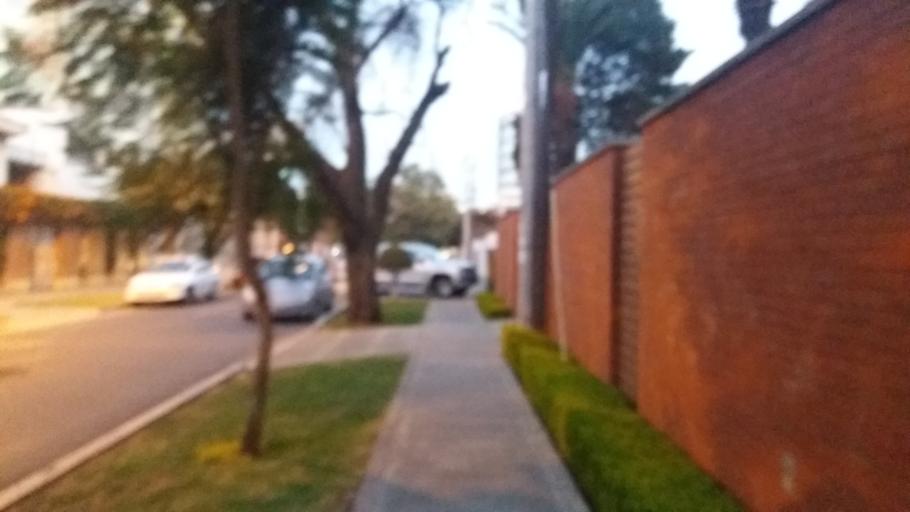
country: BO
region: Cochabamba
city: Cochabamba
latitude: -17.3846
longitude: -66.1519
